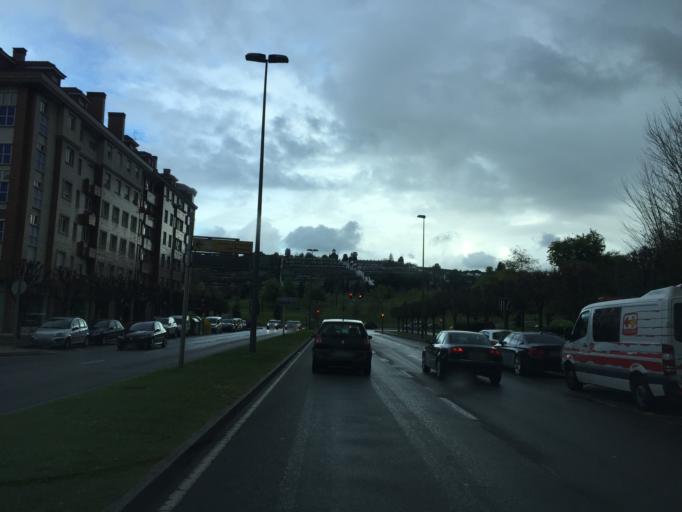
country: ES
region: Asturias
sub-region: Province of Asturias
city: Gijon
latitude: 43.5255
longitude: -5.6648
